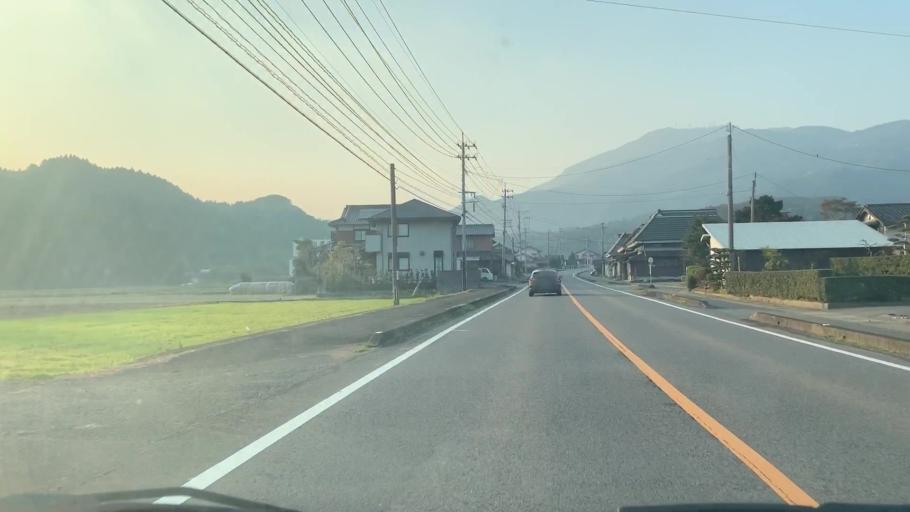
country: JP
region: Saga Prefecture
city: Takeocho-takeo
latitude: 33.2604
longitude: 130.0615
